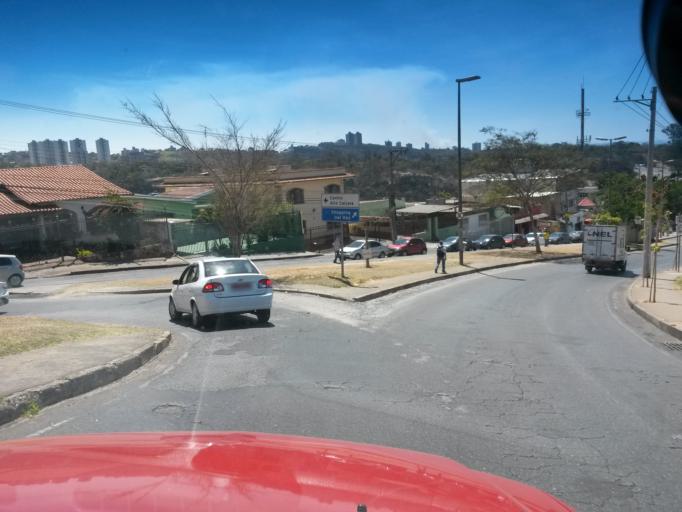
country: BR
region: Minas Gerais
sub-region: Belo Horizonte
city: Belo Horizonte
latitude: -19.8918
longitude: -43.9687
